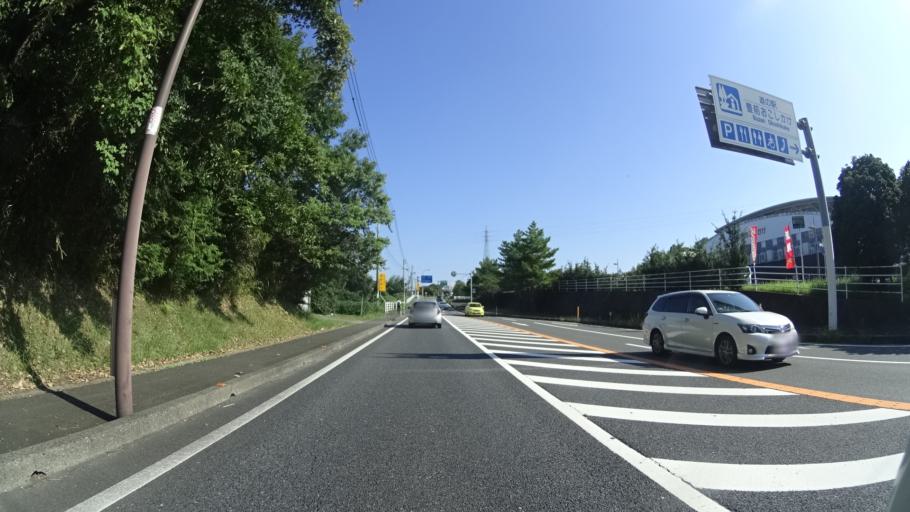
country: JP
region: Fukuoka
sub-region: Buzen-shi
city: Buzen
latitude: 33.6146
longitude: 131.1012
